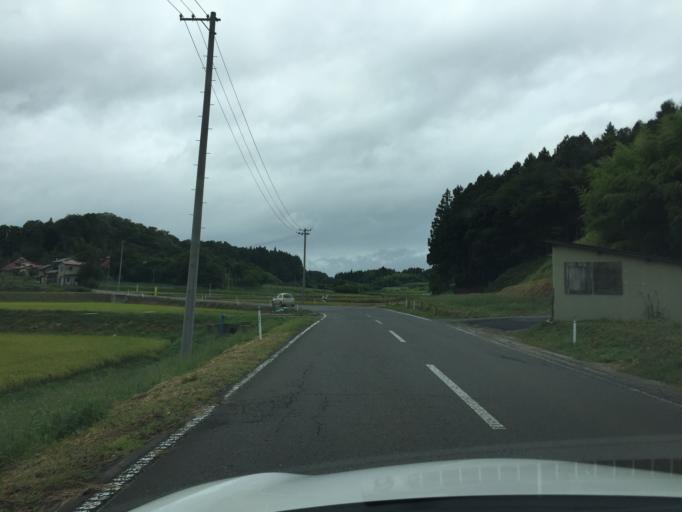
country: JP
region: Fukushima
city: Funehikimachi-funehiki
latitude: 37.4631
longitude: 140.5533
